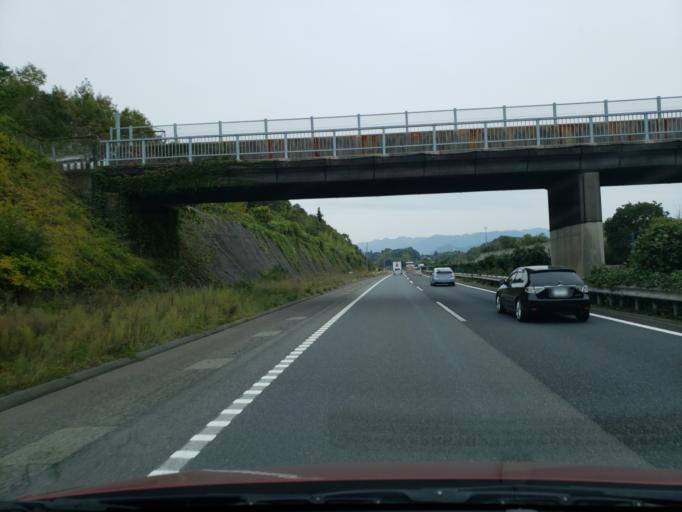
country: JP
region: Hyogo
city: Sandacho
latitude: 34.8296
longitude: 135.1690
